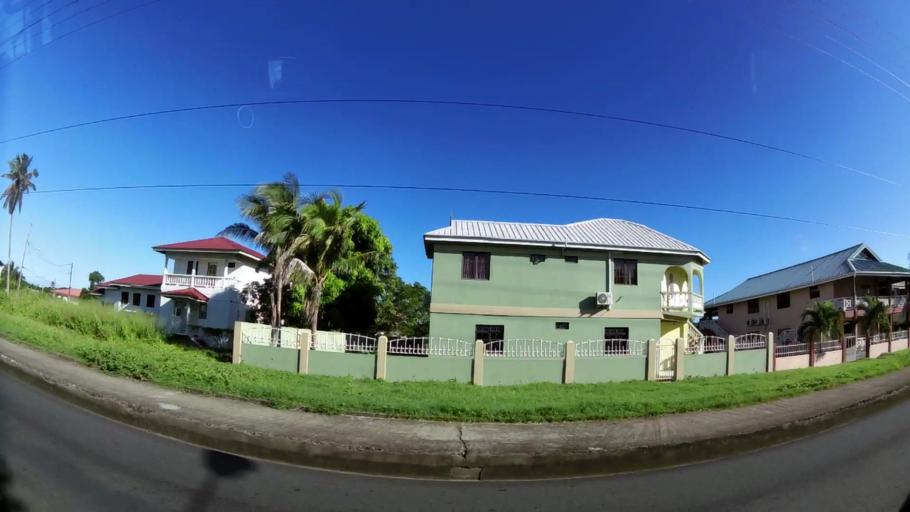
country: TT
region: Tobago
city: Scarborough
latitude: 11.1579
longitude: -60.8256
